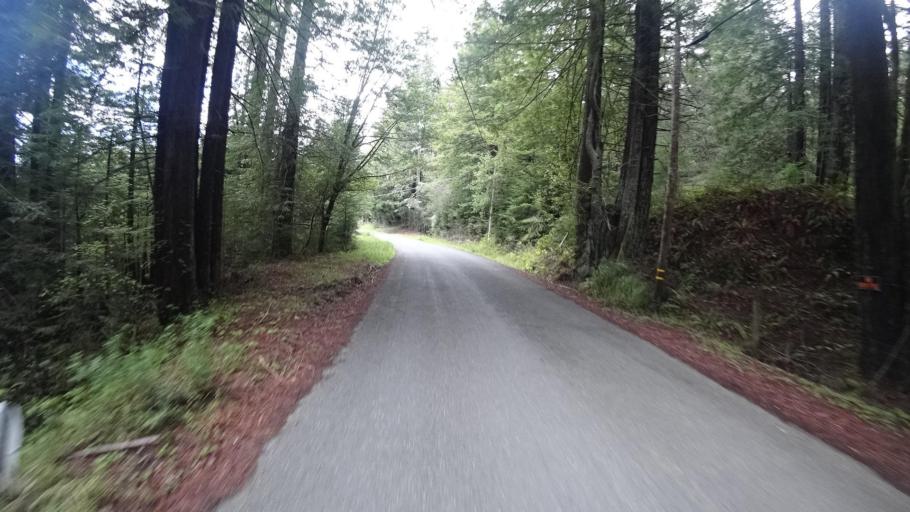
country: US
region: California
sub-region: Humboldt County
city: Blue Lake
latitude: 40.8538
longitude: -123.9292
